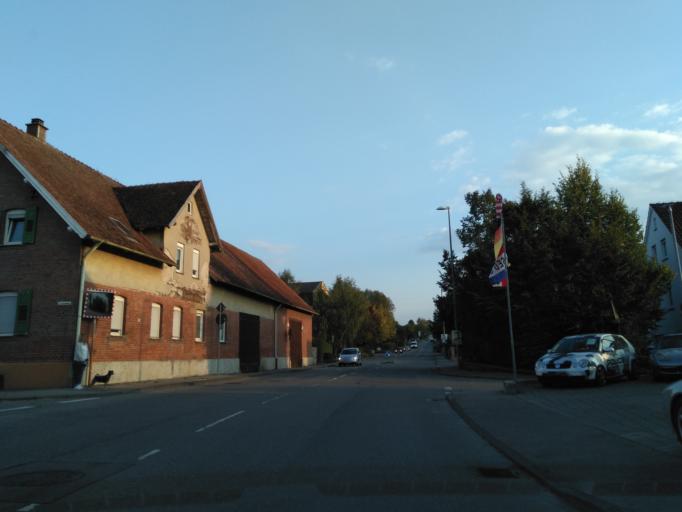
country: DE
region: Baden-Wuerttemberg
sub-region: Regierungsbezirk Stuttgart
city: Markgroningen
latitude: 48.9009
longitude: 9.0851
